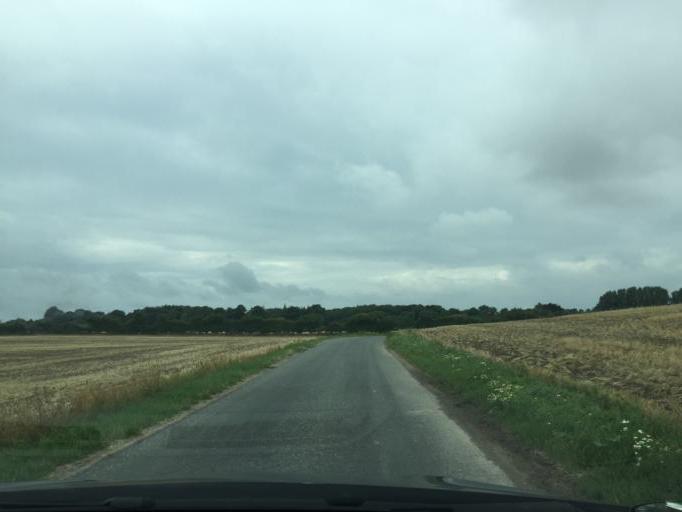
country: DK
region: South Denmark
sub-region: Assens Kommune
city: Harby
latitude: 55.1955
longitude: 10.0483
